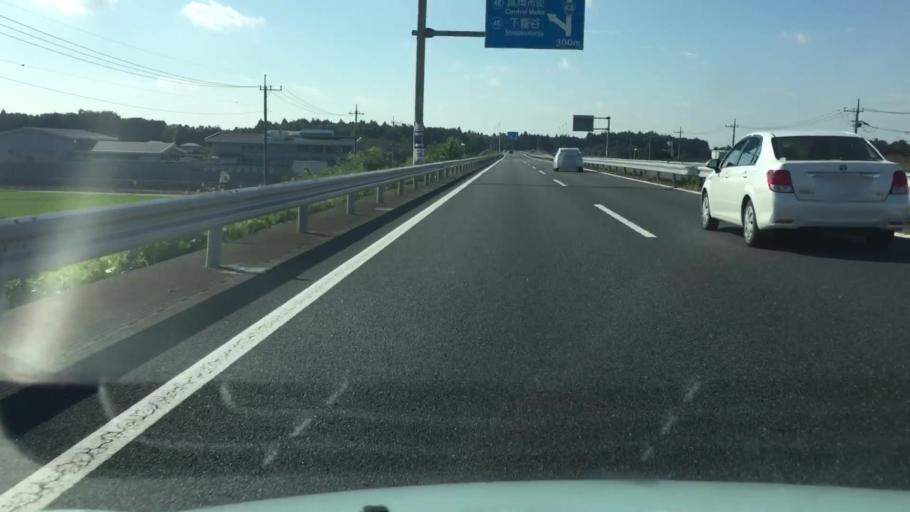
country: JP
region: Tochigi
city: Mooka
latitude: 36.4764
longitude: 139.9906
